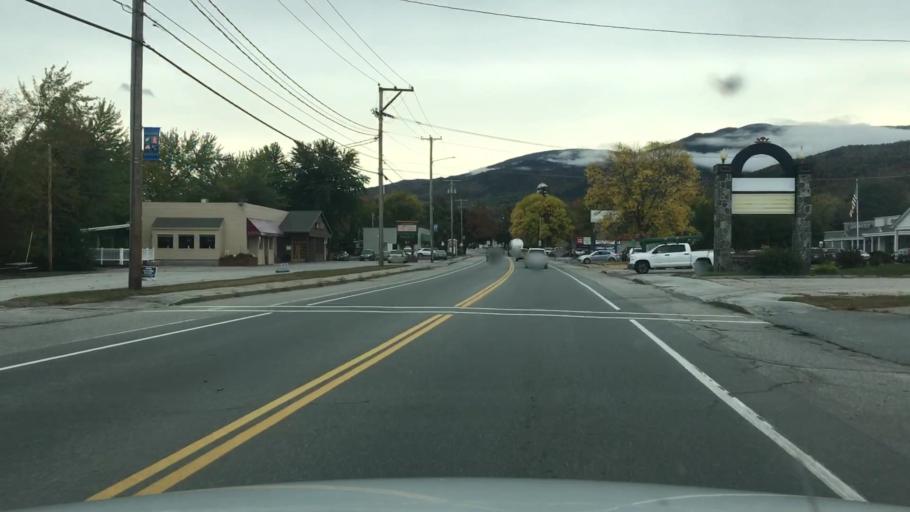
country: US
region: New Hampshire
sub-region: Coos County
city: Gorham
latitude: 44.3909
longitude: -71.1830
